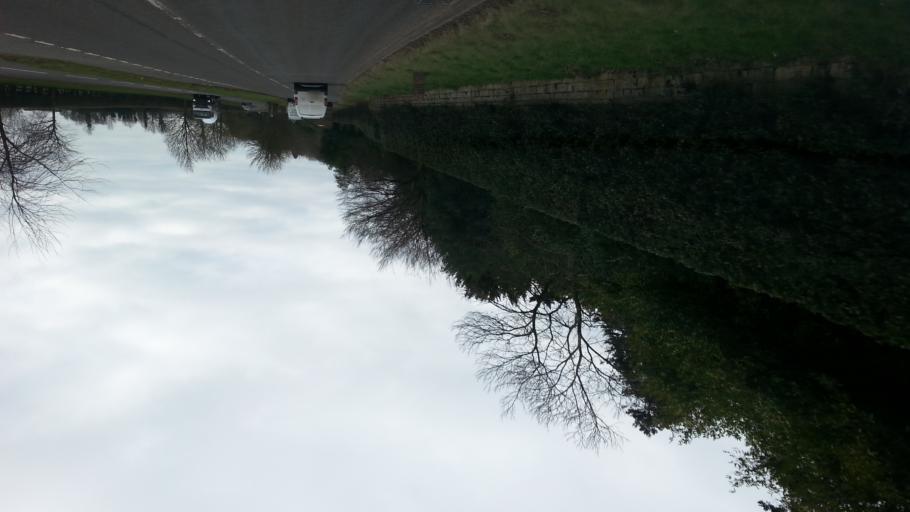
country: GB
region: England
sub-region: Staffordshire
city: Stafford
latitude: 52.8534
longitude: -2.0671
